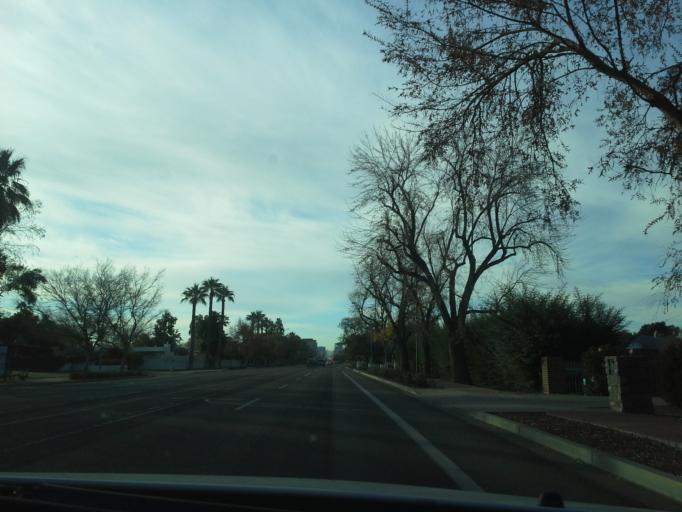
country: US
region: Arizona
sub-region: Maricopa County
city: Phoenix
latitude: 33.5210
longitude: -112.0738
